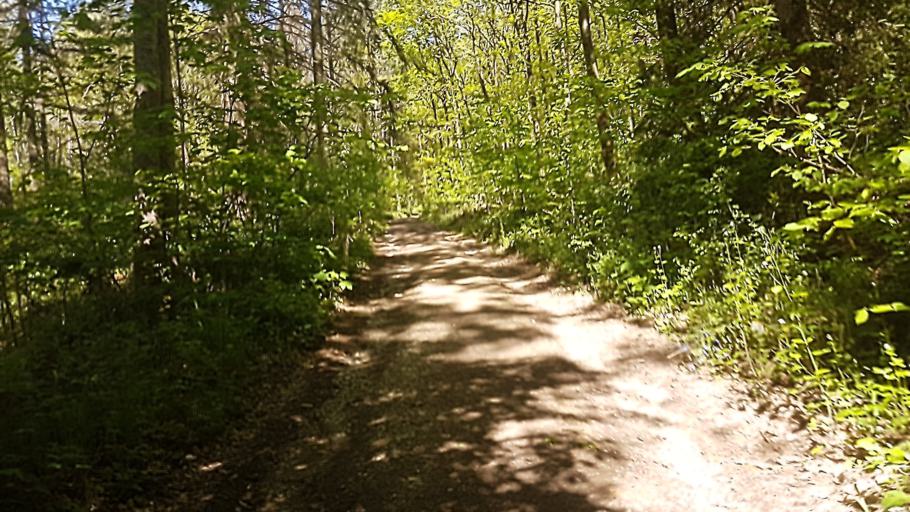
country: BE
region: Wallonia
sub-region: Province de Namur
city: Couvin
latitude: 50.0584
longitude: 4.5998
